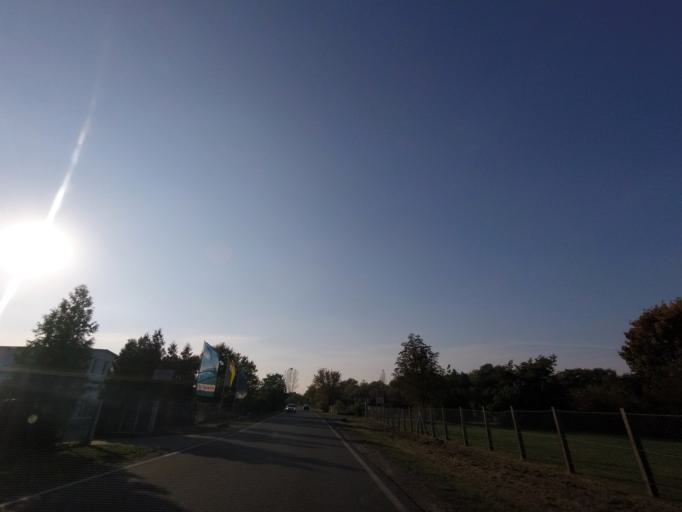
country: DE
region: Saxony-Anhalt
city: Jessen
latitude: 51.8018
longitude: 12.9401
